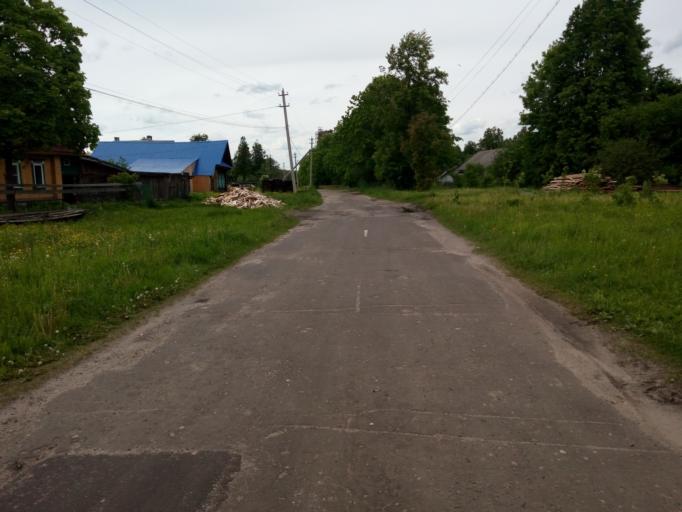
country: RU
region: Nizjnij Novgorod
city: Voskresenskoye
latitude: 56.7778
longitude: 45.5394
